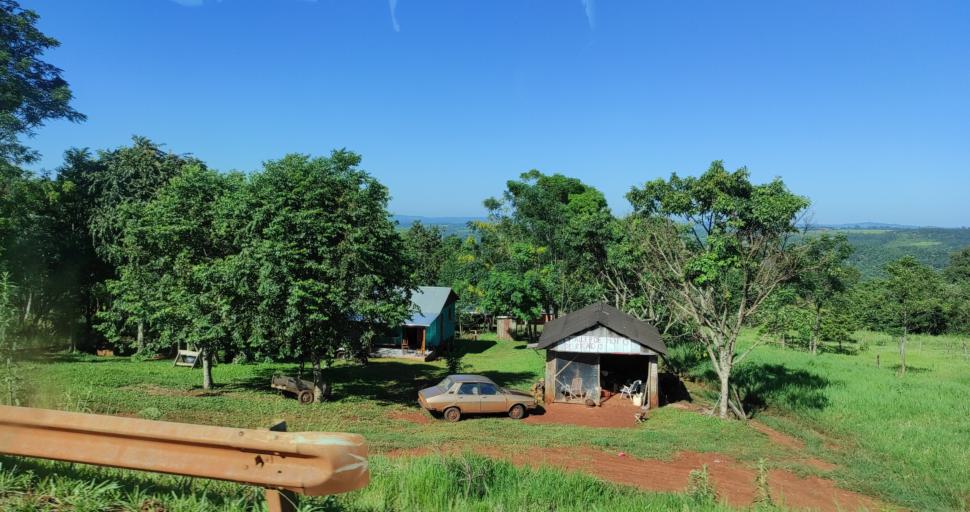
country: AR
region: Misiones
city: El Soberbio
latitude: -27.1859
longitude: -54.1067
